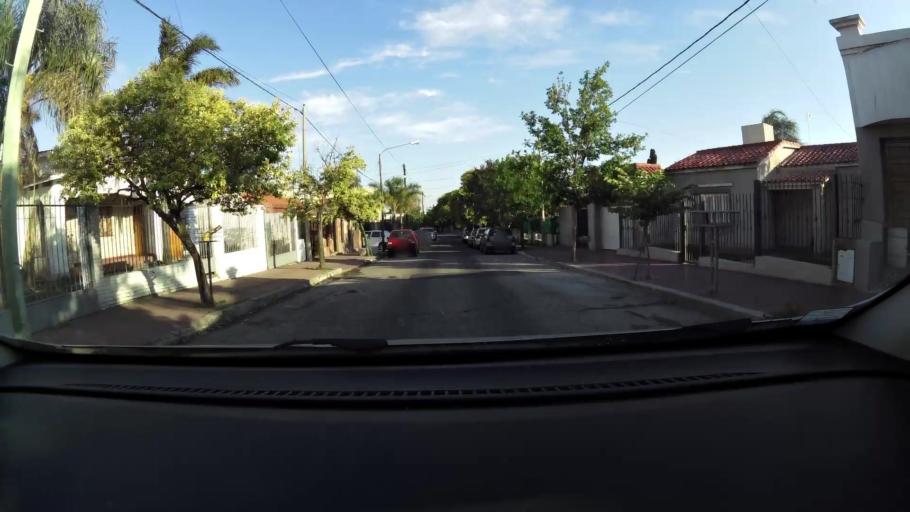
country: AR
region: Cordoba
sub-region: Departamento de Capital
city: Cordoba
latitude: -31.3837
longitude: -64.2235
